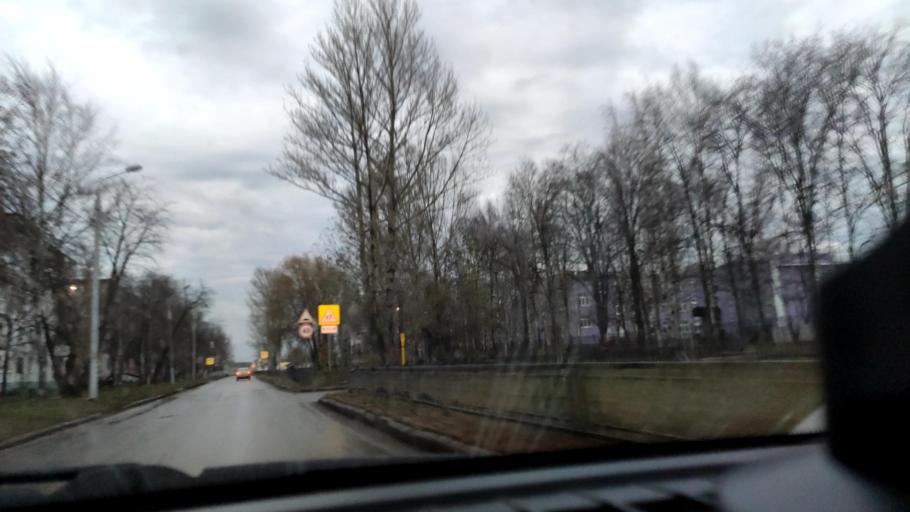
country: RU
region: Perm
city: Perm
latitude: 57.9951
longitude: 56.2987
